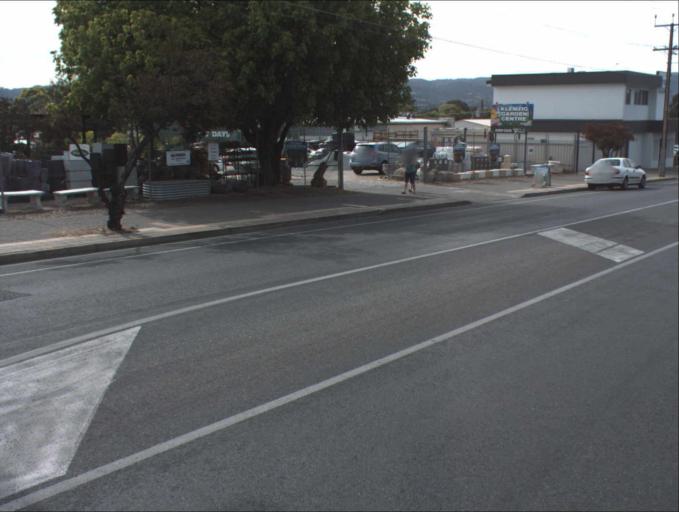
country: AU
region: South Australia
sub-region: Port Adelaide Enfield
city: Klemzig
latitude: -34.8774
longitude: 138.6342
